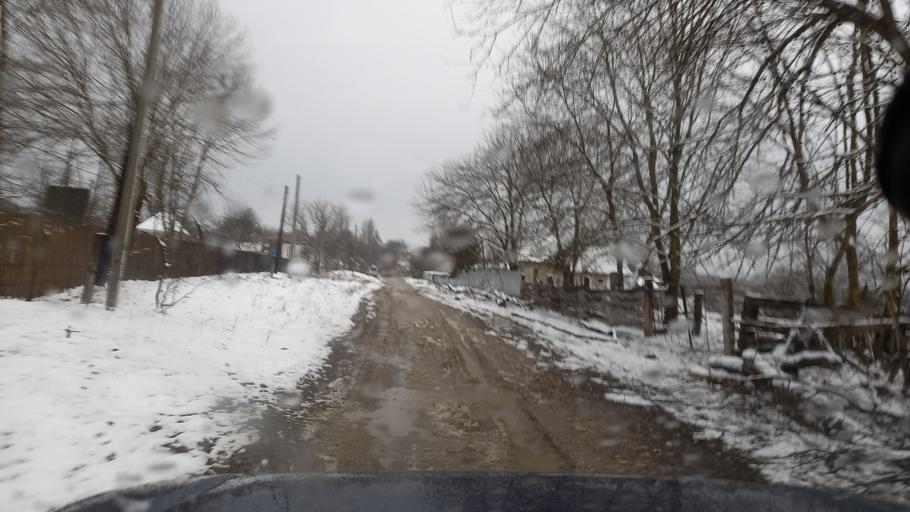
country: RU
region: Adygeya
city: Abadzekhskaya
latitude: 44.3535
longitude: 40.4172
